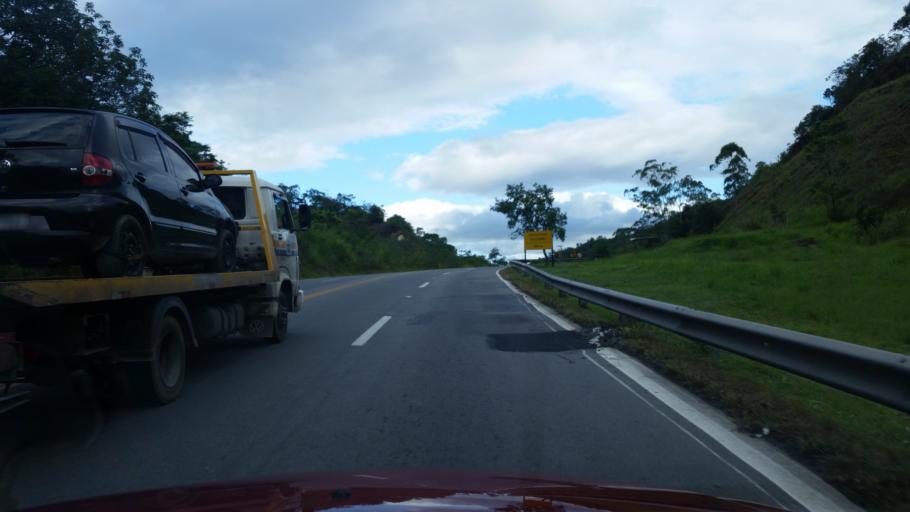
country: BR
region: Sao Paulo
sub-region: Miracatu
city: Miracatu
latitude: -24.2690
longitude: -47.2875
